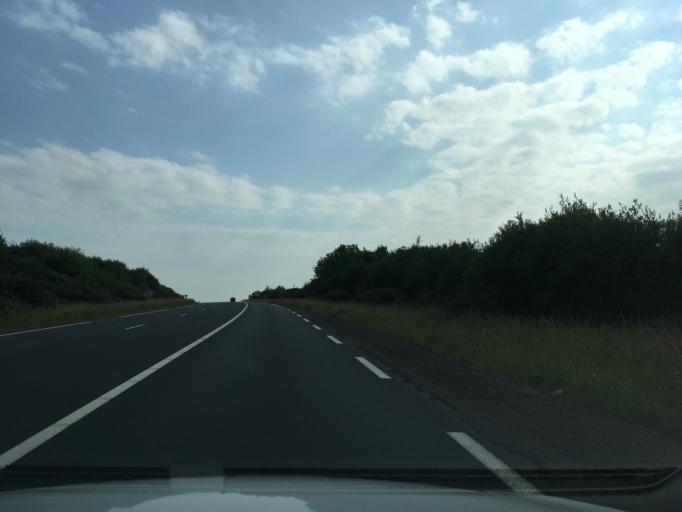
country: FR
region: Poitou-Charentes
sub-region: Departement des Deux-Sevres
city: Saint-Pardoux
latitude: 46.5224
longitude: -0.3271
